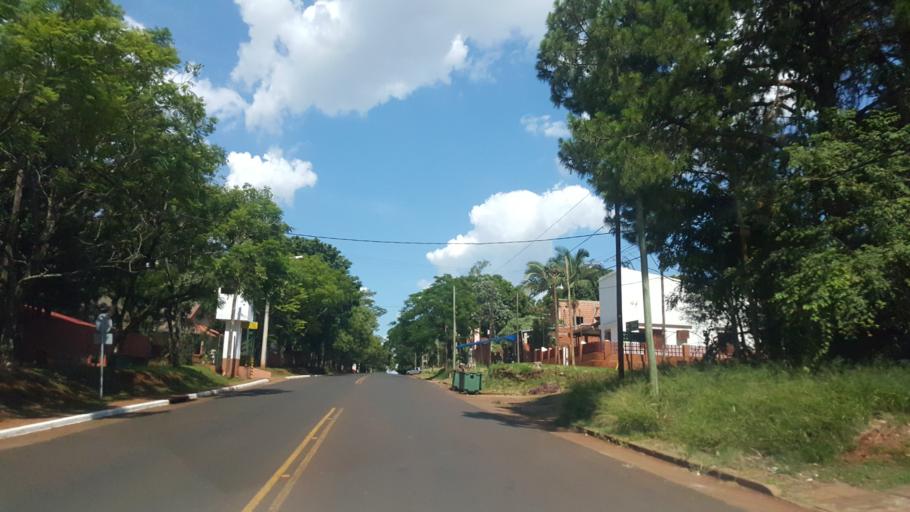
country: AR
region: Misiones
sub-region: Departamento de Capital
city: Posadas
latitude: -27.3648
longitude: -55.9230
